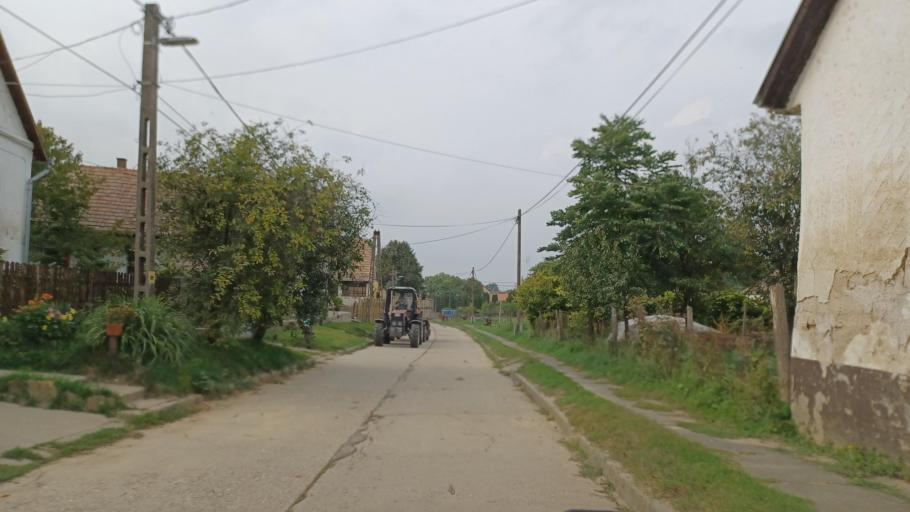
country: HU
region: Tolna
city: Gyonk
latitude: 46.5707
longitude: 18.4273
